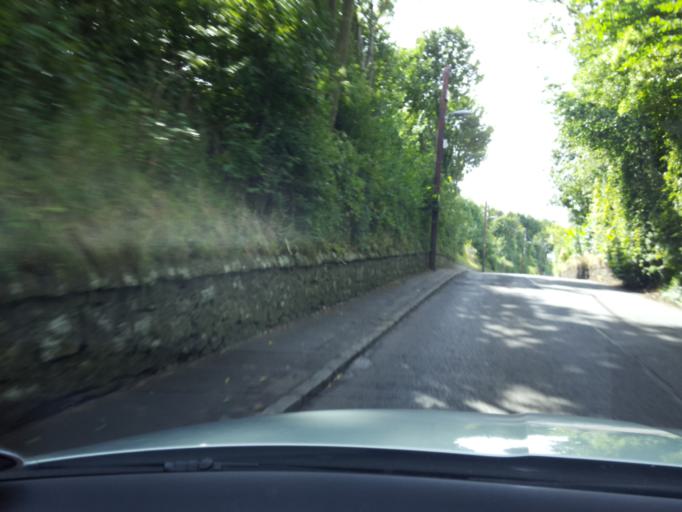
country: GB
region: Scotland
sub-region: Falkirk
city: Bo'ness
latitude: 56.0113
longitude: -3.5757
